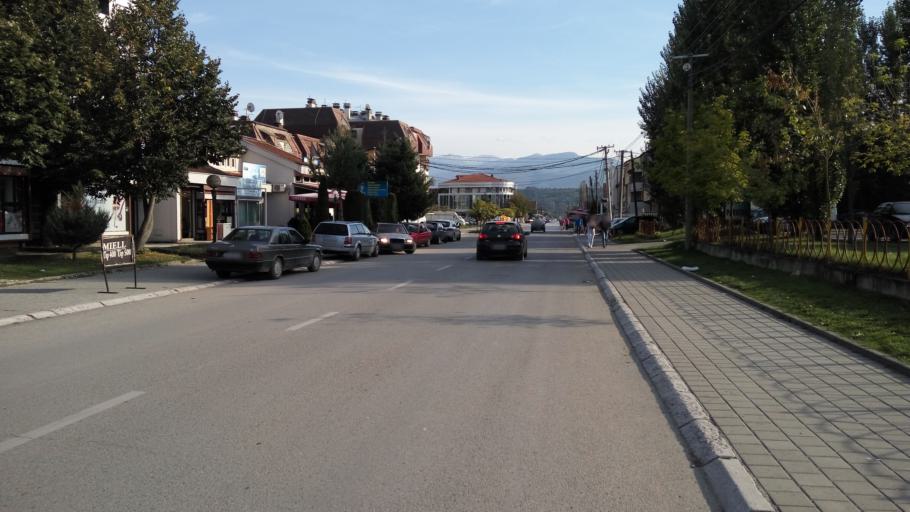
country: XK
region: Gjakova
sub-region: Komuna e Gjakoves
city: Gjakove
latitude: 42.3738
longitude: 20.4337
